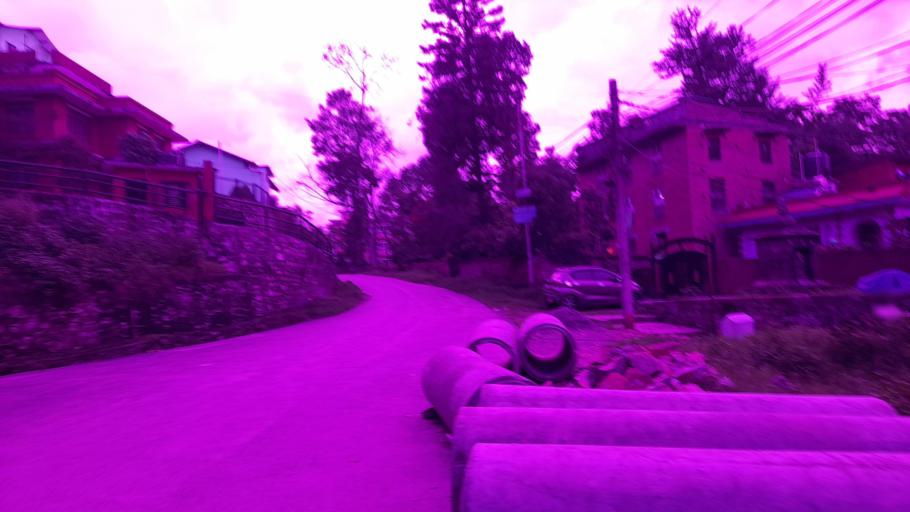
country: NP
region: Central Region
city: Banepa
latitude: 27.6150
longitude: 85.5649
